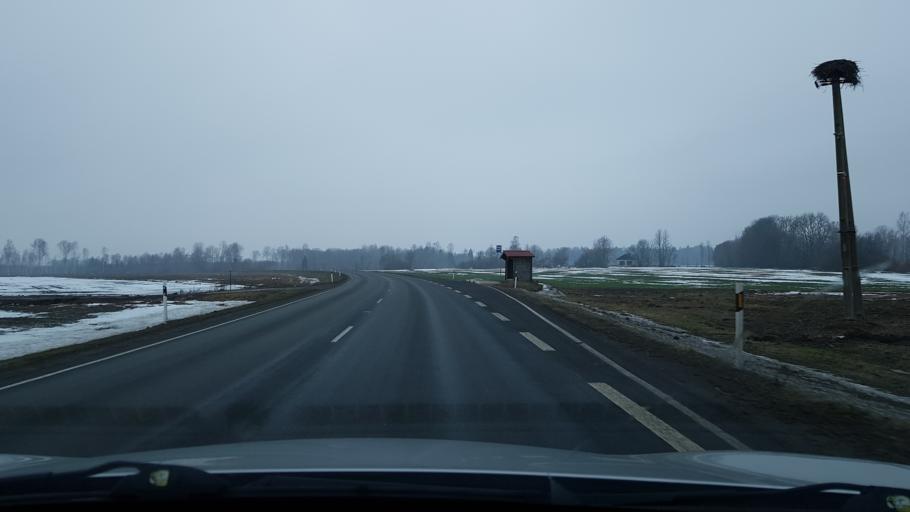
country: EE
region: Jogevamaa
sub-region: Poltsamaa linn
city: Poltsamaa
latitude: 58.3947
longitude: 25.9144
